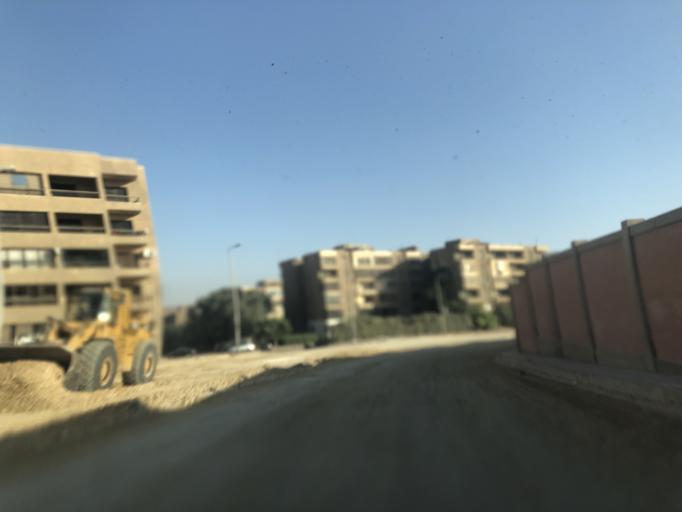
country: EG
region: Al Jizah
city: Al Jizah
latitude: 29.9864
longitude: 31.1125
